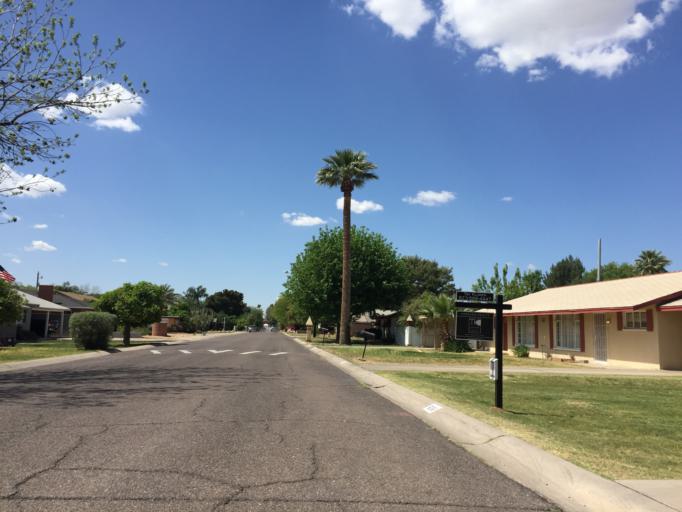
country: US
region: Arizona
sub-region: Maricopa County
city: Phoenix
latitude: 33.5329
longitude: -112.0612
